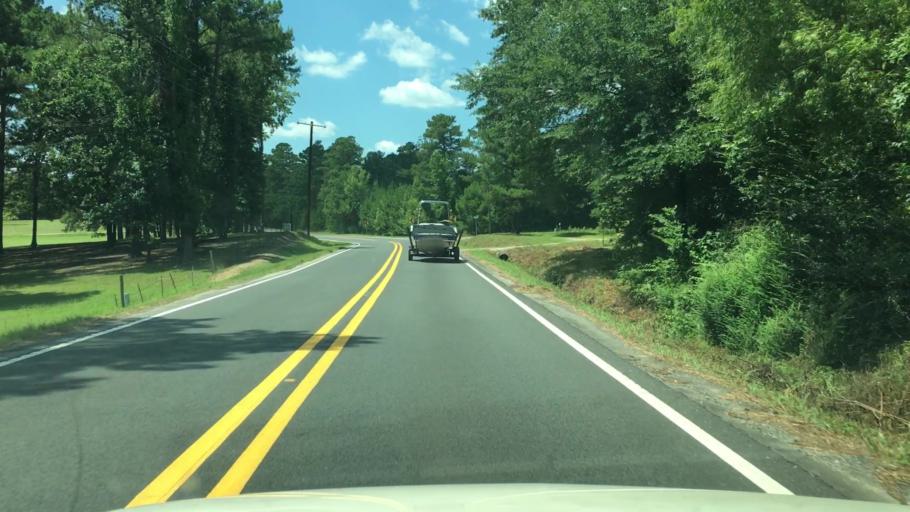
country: US
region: Arkansas
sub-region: Clark County
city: Arkadelphia
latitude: 34.2533
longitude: -93.1235
